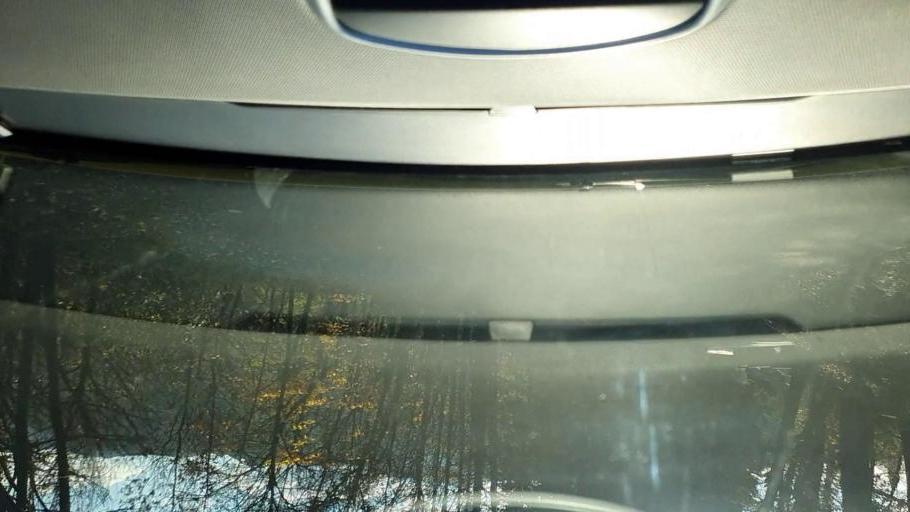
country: FR
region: Languedoc-Roussillon
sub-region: Departement du Gard
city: Branoux-les-Taillades
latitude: 44.2539
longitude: 3.9763
